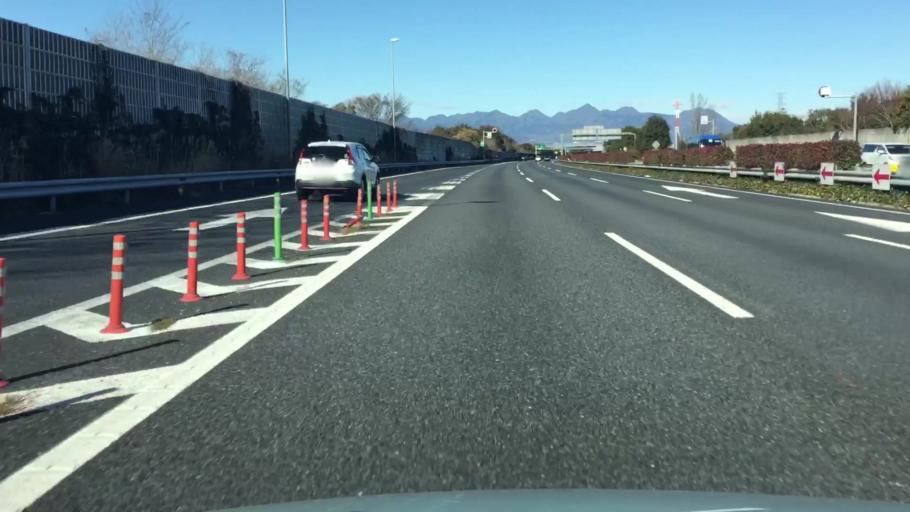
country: JP
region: Gunma
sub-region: Sawa-gun
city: Tamamura
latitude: 36.3239
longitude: 139.0707
